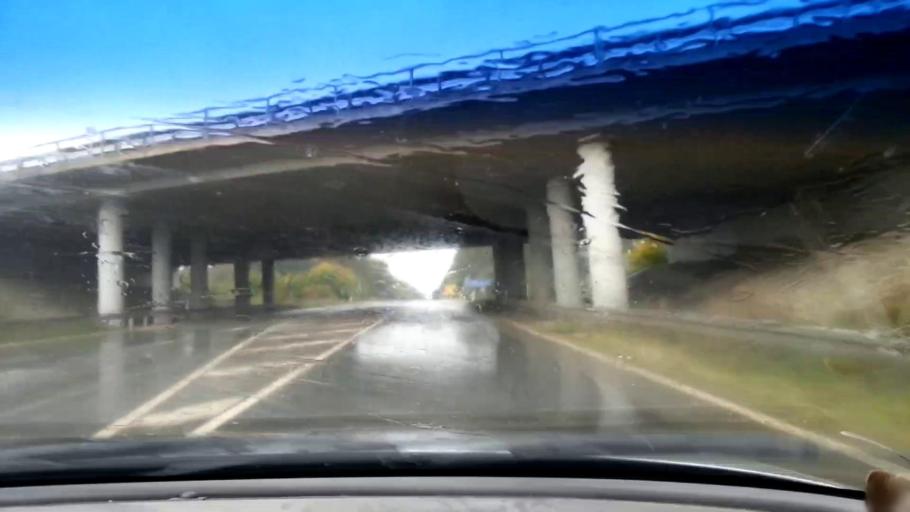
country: DE
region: Bavaria
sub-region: Upper Franconia
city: Stadelhofen
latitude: 50.0001
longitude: 11.2083
